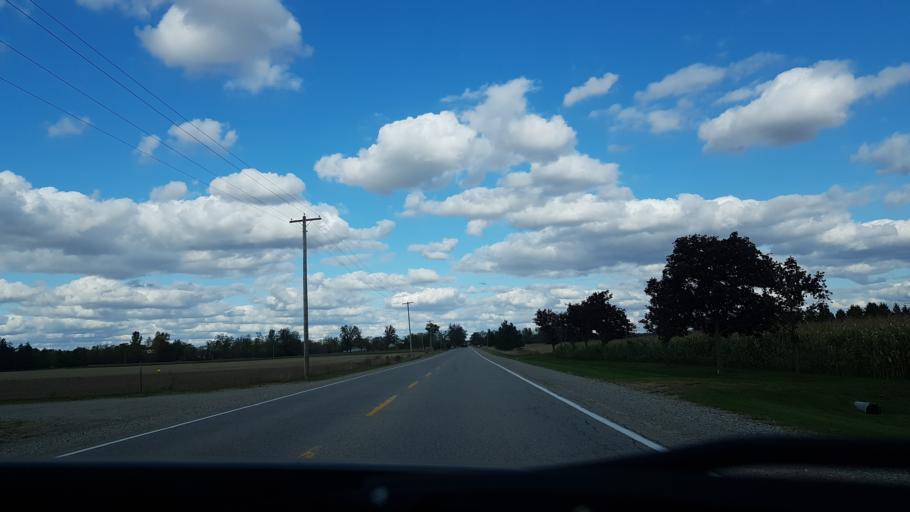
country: CA
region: Ontario
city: South Huron
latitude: 43.0938
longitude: -81.5726
